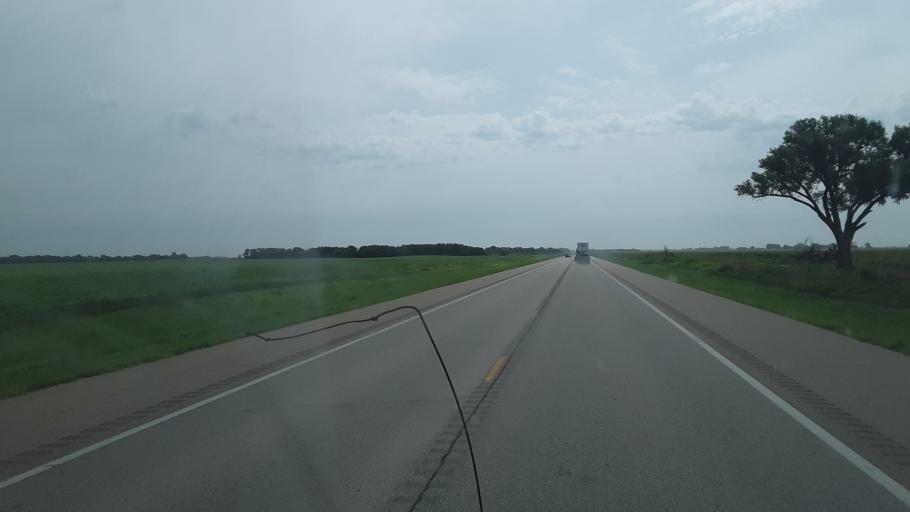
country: US
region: Kansas
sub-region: Reno County
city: Nickerson
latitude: 37.9850
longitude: -98.2233
